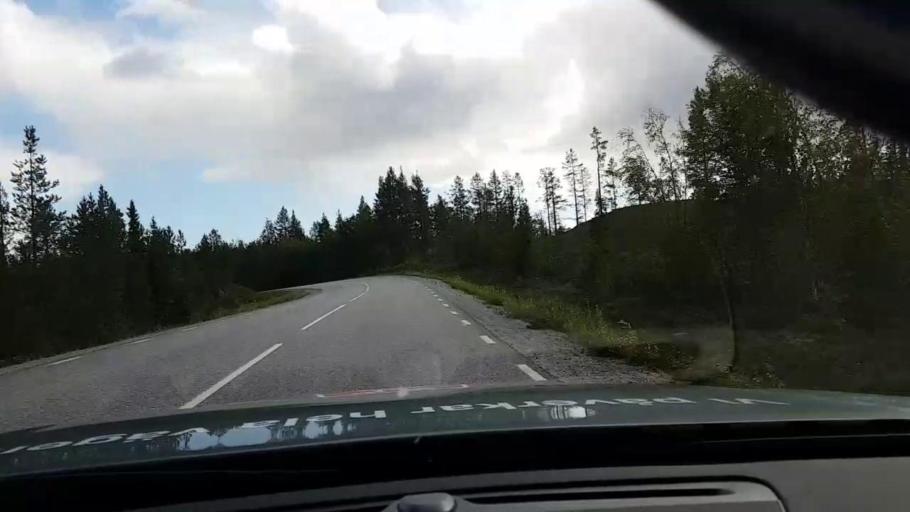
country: SE
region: Vaesternorrland
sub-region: OErnskoeldsviks Kommun
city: Bredbyn
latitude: 63.6778
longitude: 17.7911
